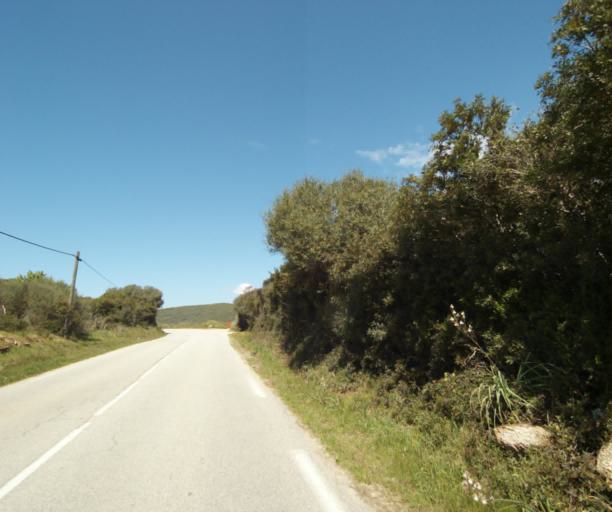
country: FR
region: Corsica
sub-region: Departement de la Corse-du-Sud
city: Propriano
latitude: 41.6582
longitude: 8.9002
